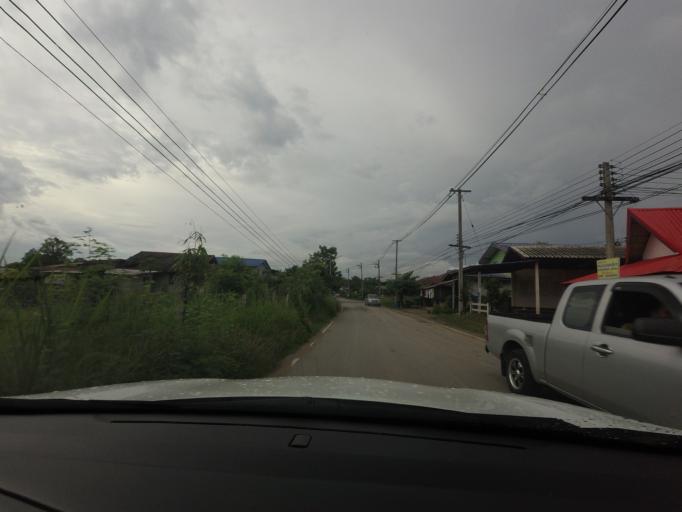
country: TH
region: Nakhon Ratchasima
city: Pak Chong
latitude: 14.6264
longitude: 101.4379
